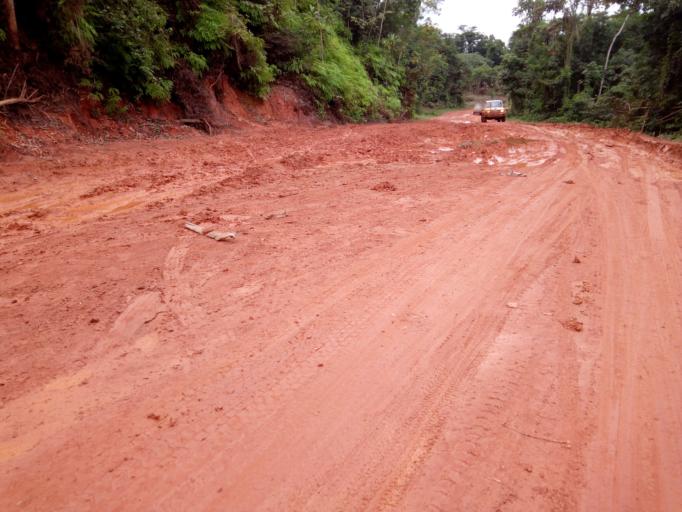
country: CI
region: Dix-Huit Montagnes
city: Toulepleu Guere
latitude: 6.4854
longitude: -8.7947
